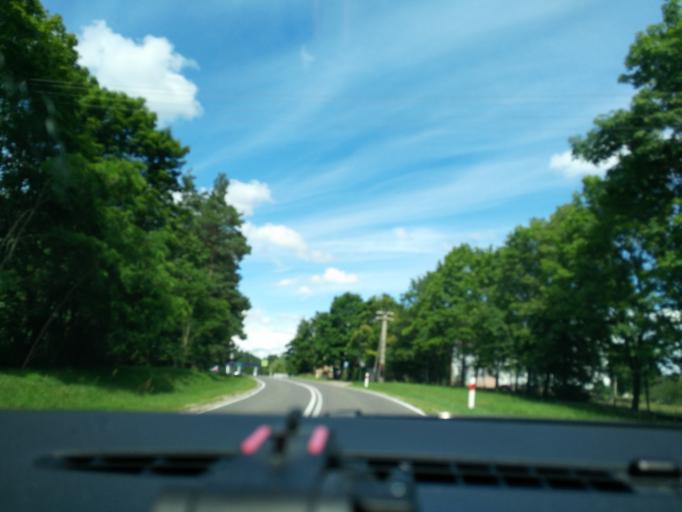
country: PL
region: Podlasie
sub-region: Powiat sejnenski
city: Sejny
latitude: 53.9803
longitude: 23.2928
